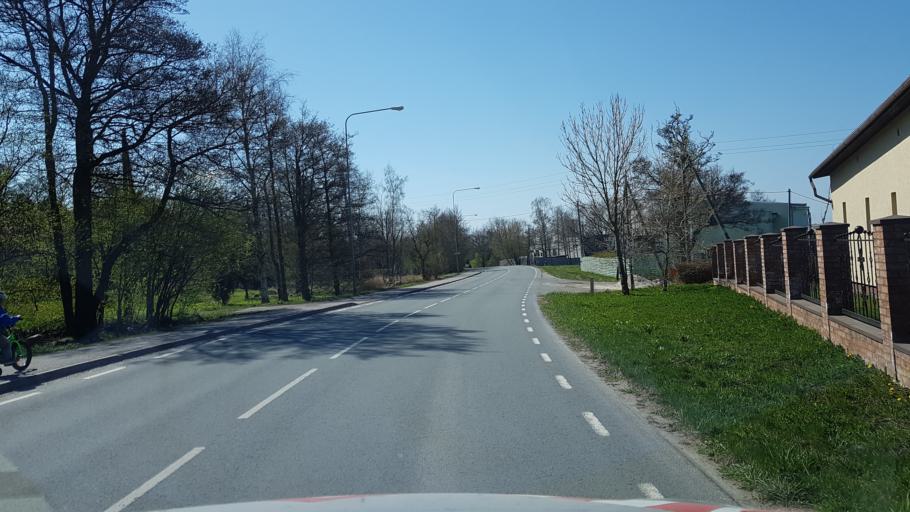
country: EE
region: Harju
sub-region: Viimsi vald
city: Rummu
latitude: 59.5604
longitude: 24.7995
